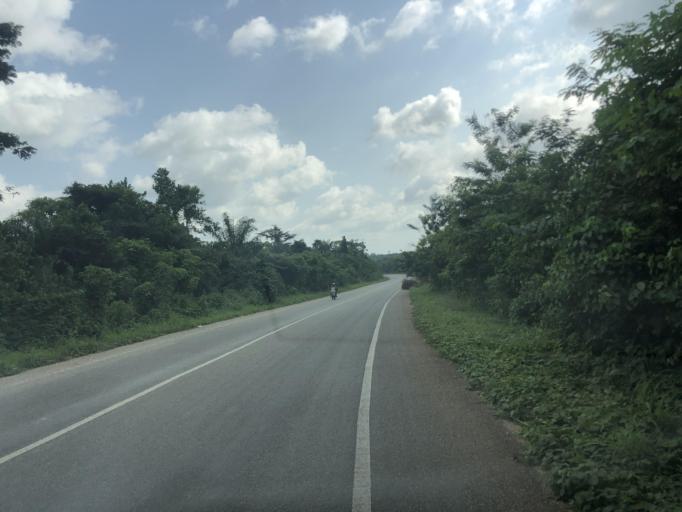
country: GH
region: Central
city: Cape Coast
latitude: 5.2259
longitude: -1.3241
